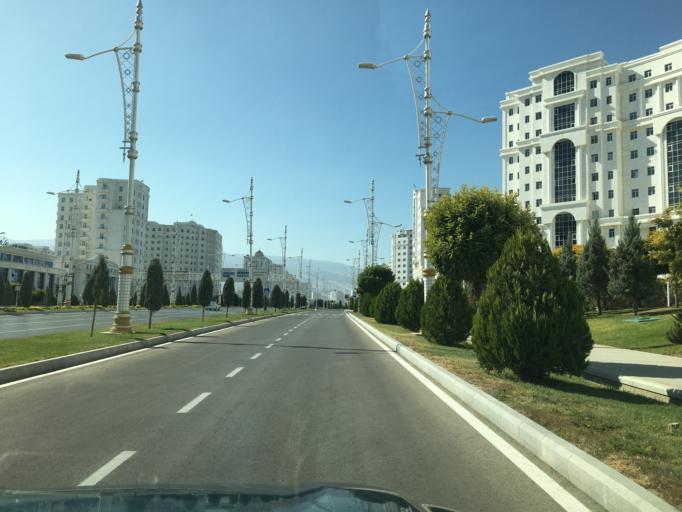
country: TM
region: Ahal
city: Ashgabat
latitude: 37.9230
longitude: 58.3630
